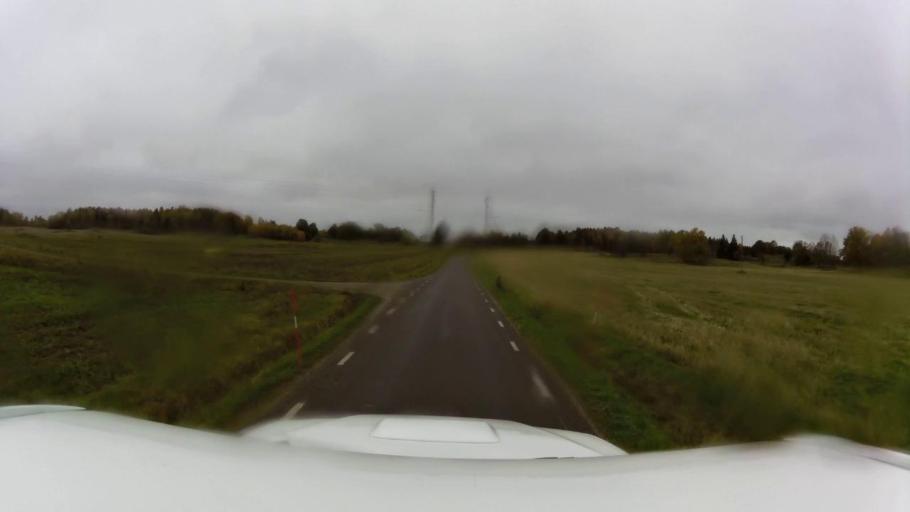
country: SE
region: OEstergoetland
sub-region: Linkopings Kommun
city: Linghem
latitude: 58.4740
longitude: 15.7917
